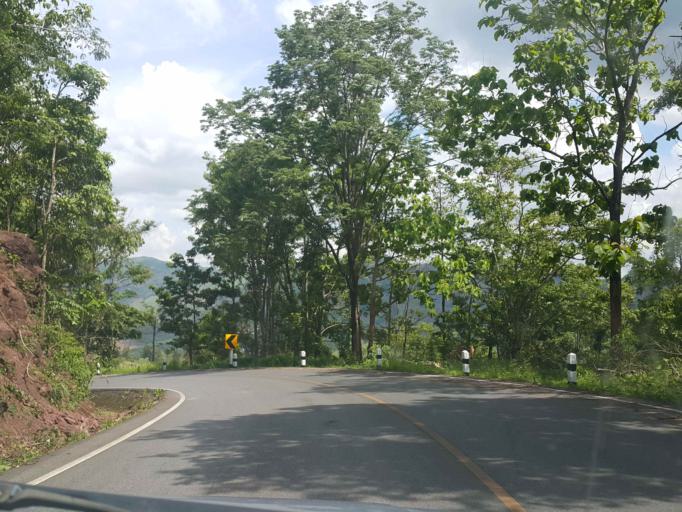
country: TH
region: Nan
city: Ban Luang
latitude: 18.8761
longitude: 100.5431
